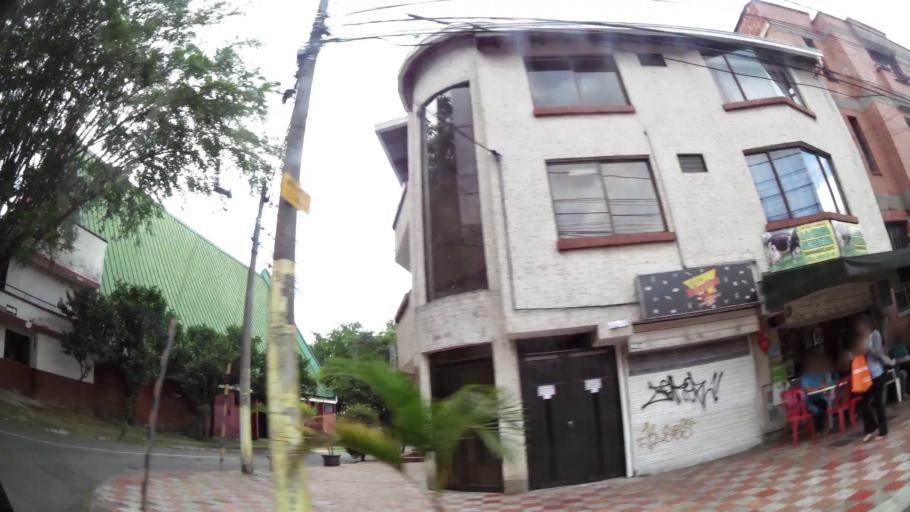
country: CO
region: Antioquia
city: Envigado
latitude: 6.1645
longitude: -75.5883
